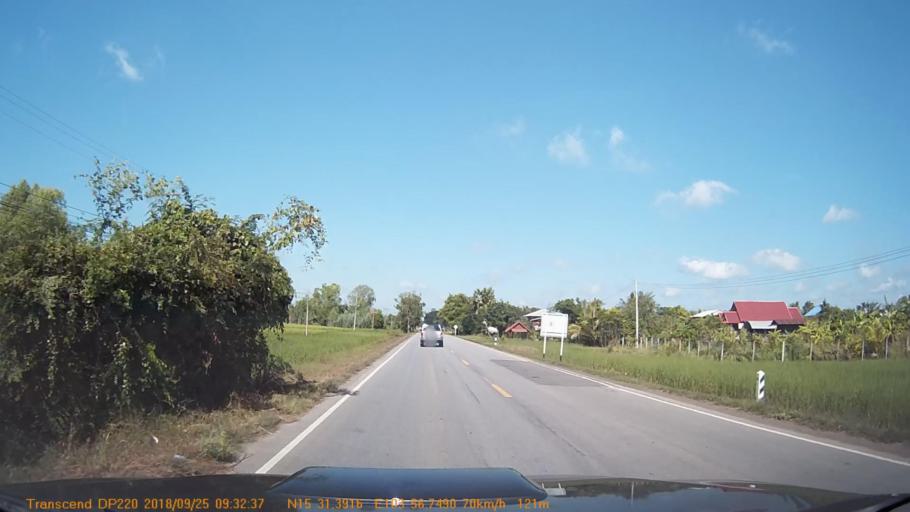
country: TH
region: Roi Et
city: Phon Sai
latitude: 15.5232
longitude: 103.9460
